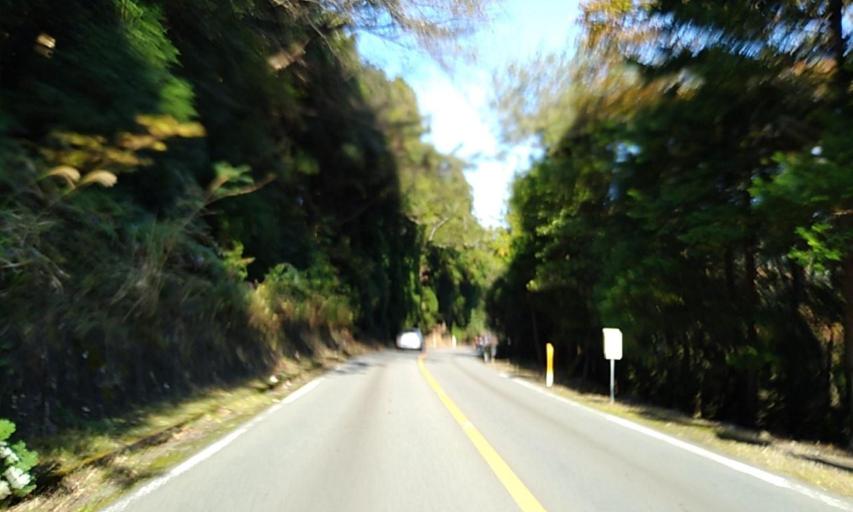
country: JP
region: Mie
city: Ise
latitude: 34.4527
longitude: 136.7434
